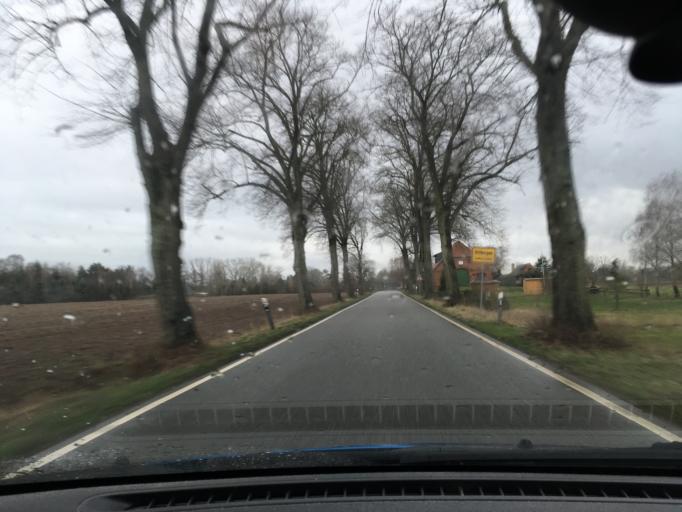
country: DE
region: Lower Saxony
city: Hittbergen
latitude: 53.3507
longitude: 10.5993
